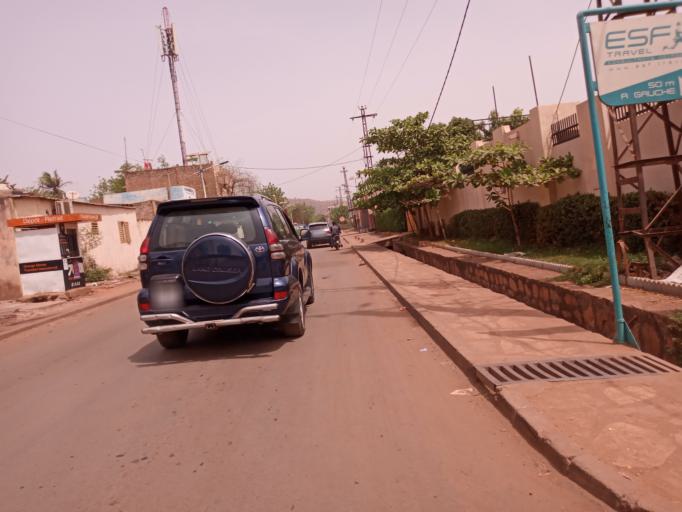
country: ML
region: Bamako
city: Bamako
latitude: 12.6457
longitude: -7.9801
